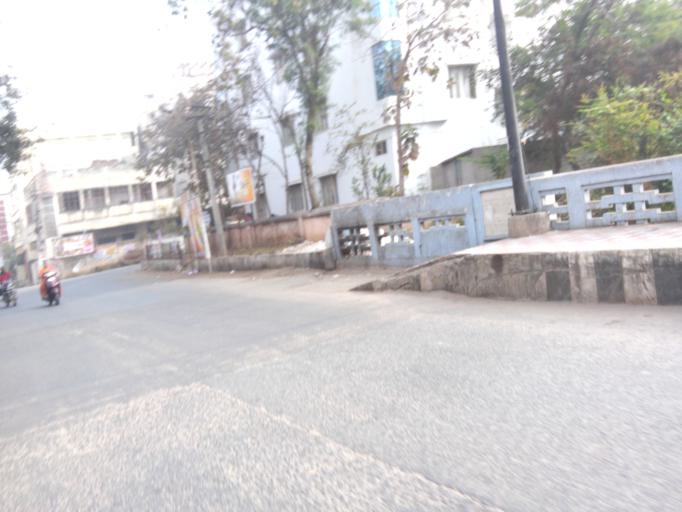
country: IN
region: Andhra Pradesh
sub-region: Krishna
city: Vijayawada
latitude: 16.5099
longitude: 80.6208
